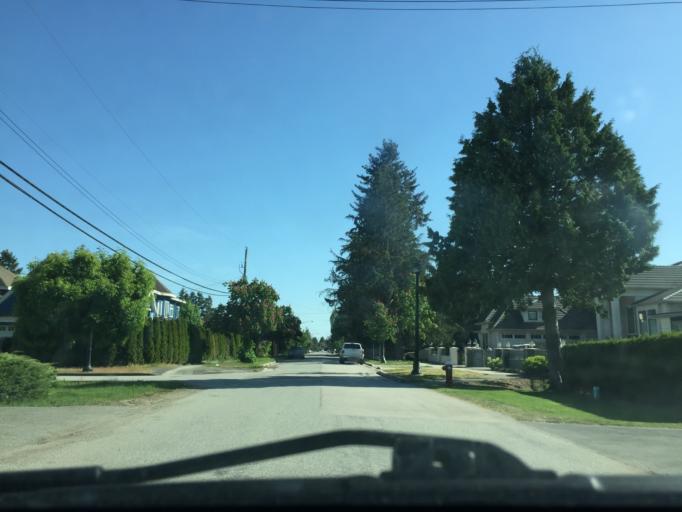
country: CA
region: British Columbia
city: Richmond
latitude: 49.1603
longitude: -123.1171
